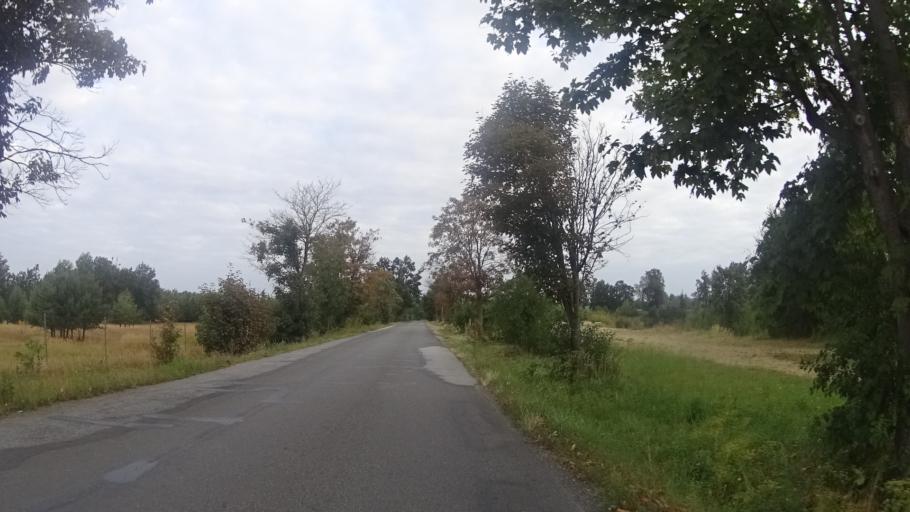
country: CZ
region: Kralovehradecky
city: Trebechovice pod Orebem
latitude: 50.2009
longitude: 15.9317
